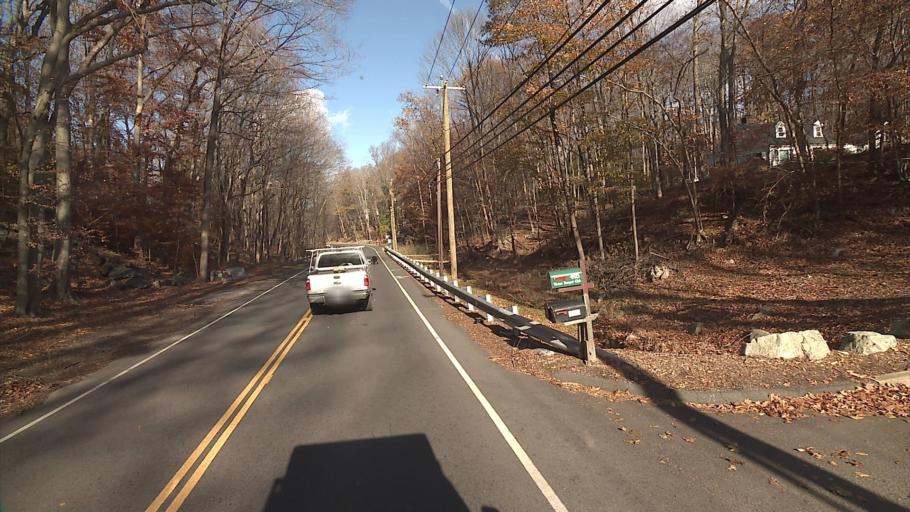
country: US
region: Connecticut
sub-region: Fairfield County
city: Georgetown
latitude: 41.2476
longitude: -73.3774
